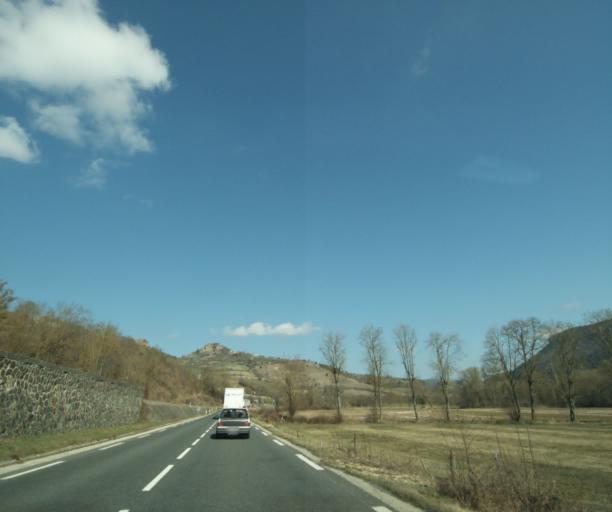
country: FR
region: Languedoc-Roussillon
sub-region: Departement de la Lozere
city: Chanac
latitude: 44.4957
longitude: 3.3962
